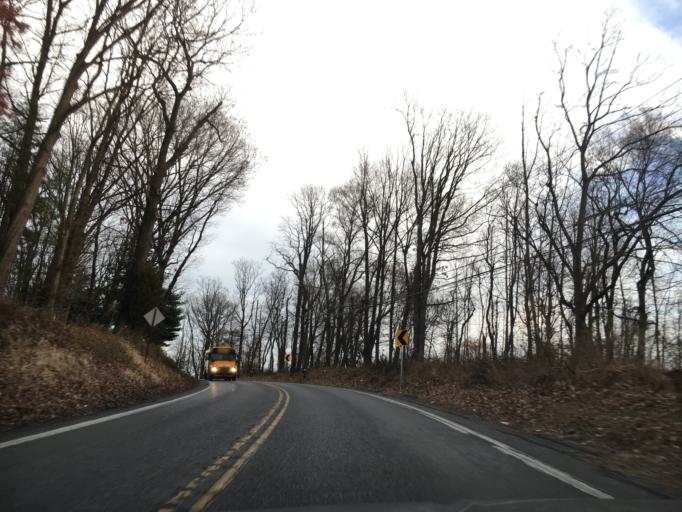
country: US
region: Pennsylvania
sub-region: Lehigh County
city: Slatington
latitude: 40.7195
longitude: -75.6082
